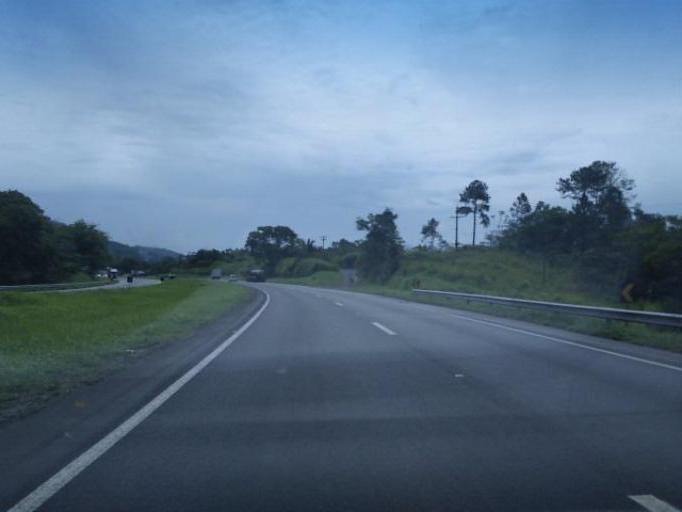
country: BR
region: Sao Paulo
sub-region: Miracatu
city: Miracatu
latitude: -24.2800
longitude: -47.4280
